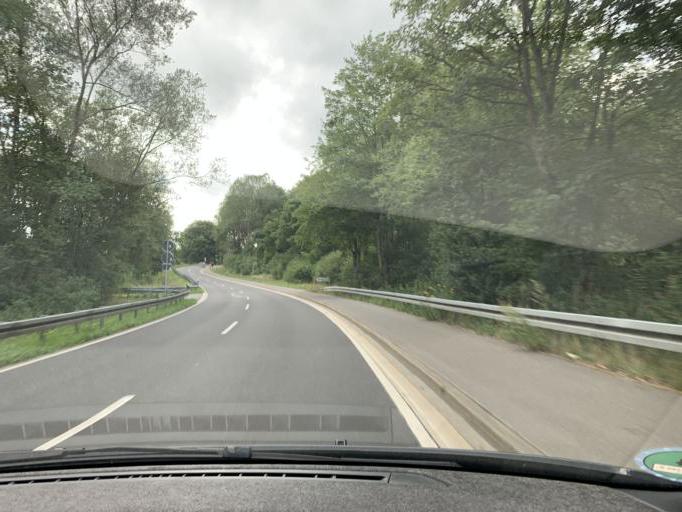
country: DE
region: North Rhine-Westphalia
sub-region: Regierungsbezirk Koln
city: Simmerath
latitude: 50.6283
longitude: 6.2950
